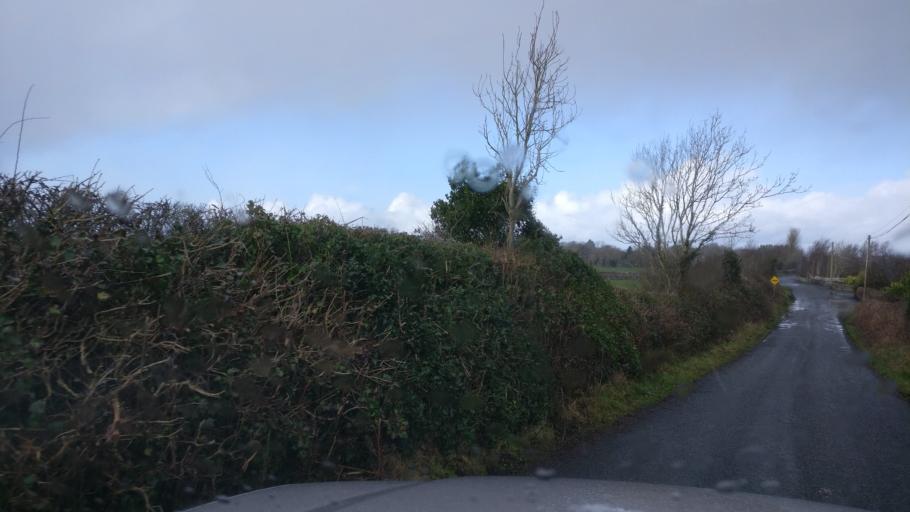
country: IE
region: Connaught
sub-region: County Galway
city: Oranmore
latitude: 53.2443
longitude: -8.8385
